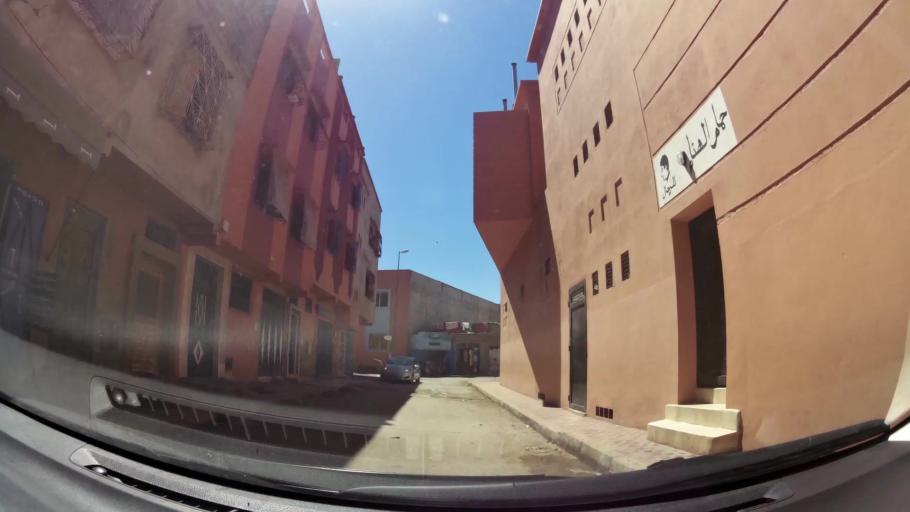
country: MA
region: Marrakech-Tensift-Al Haouz
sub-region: Marrakech
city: Marrakesh
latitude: 31.5726
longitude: -7.9826
